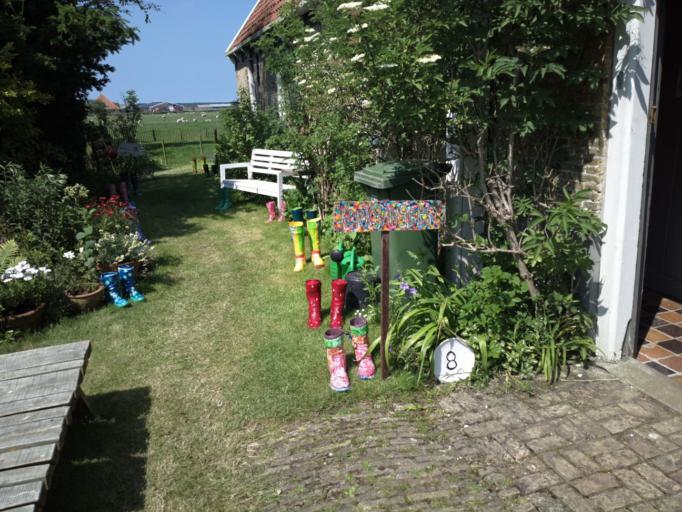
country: NL
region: North Holland
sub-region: Gemeente Texel
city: Den Burg
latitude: 53.0258
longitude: 4.7535
